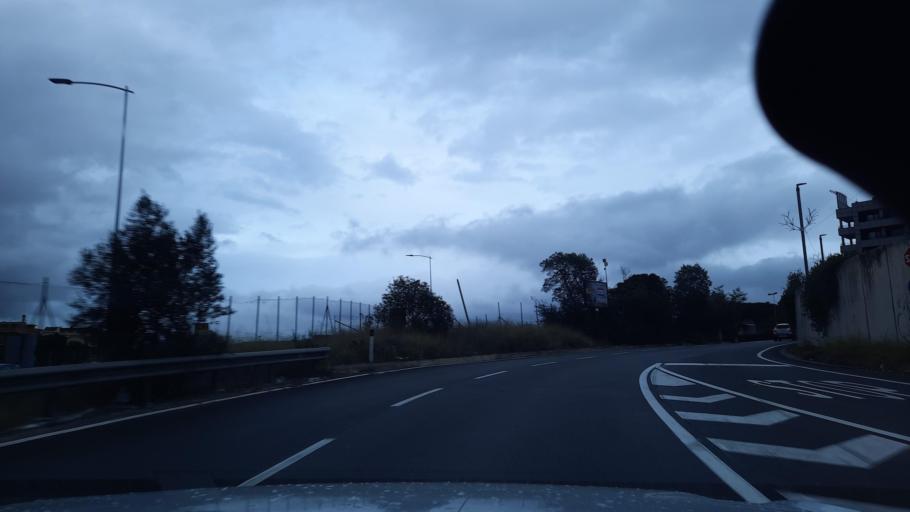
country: IT
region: Latium
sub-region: Citta metropolitana di Roma Capitale
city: Ciampino
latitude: 41.8500
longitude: 12.6056
